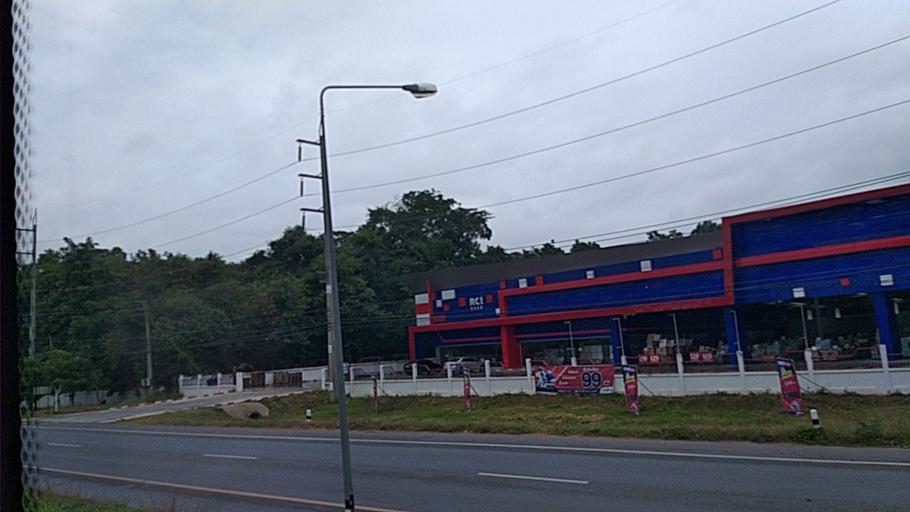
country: TH
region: Maha Sarakham
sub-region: Amphoe Borabue
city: Borabue
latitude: 16.0477
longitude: 103.1261
